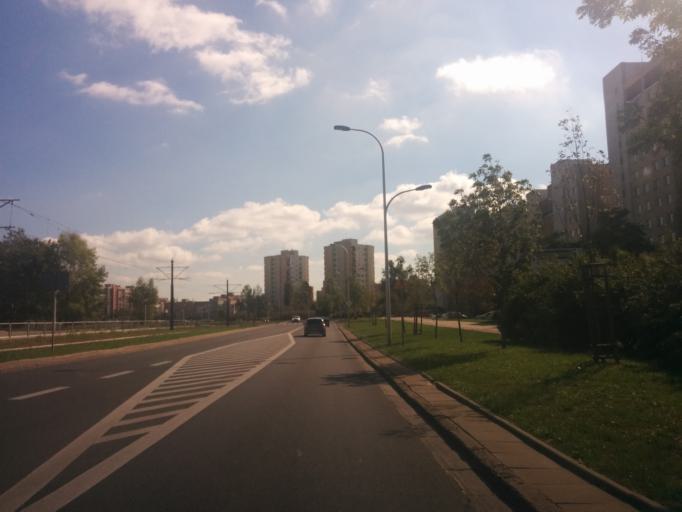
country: PL
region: Masovian Voivodeship
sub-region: Warszawa
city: Bialoleka
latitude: 52.3177
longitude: 20.9540
